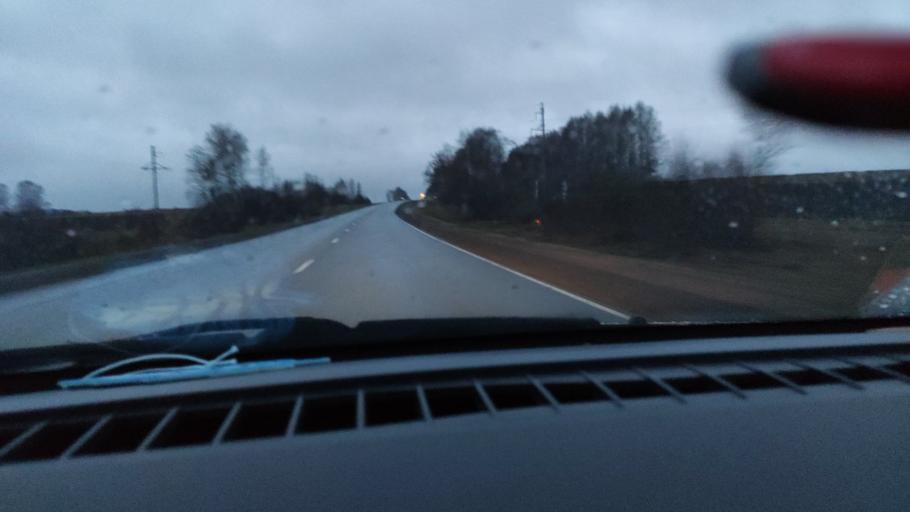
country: RU
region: Udmurtiya
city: Mozhga
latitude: 56.3194
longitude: 52.3237
